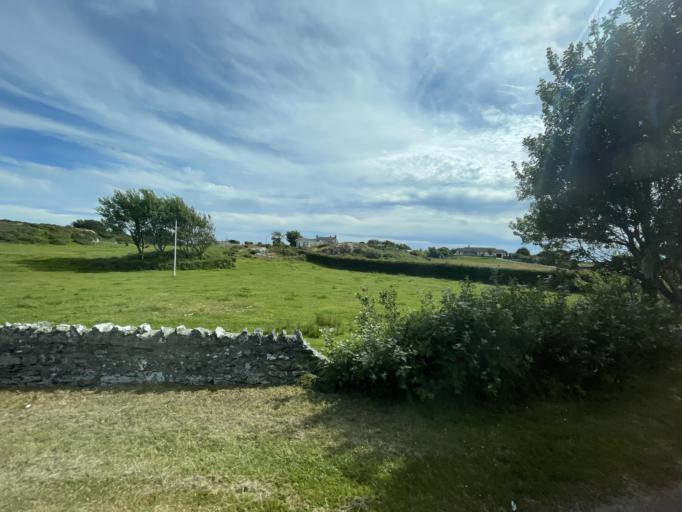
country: GB
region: Wales
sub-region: Anglesey
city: Valley
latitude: 53.2707
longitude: -4.5929
